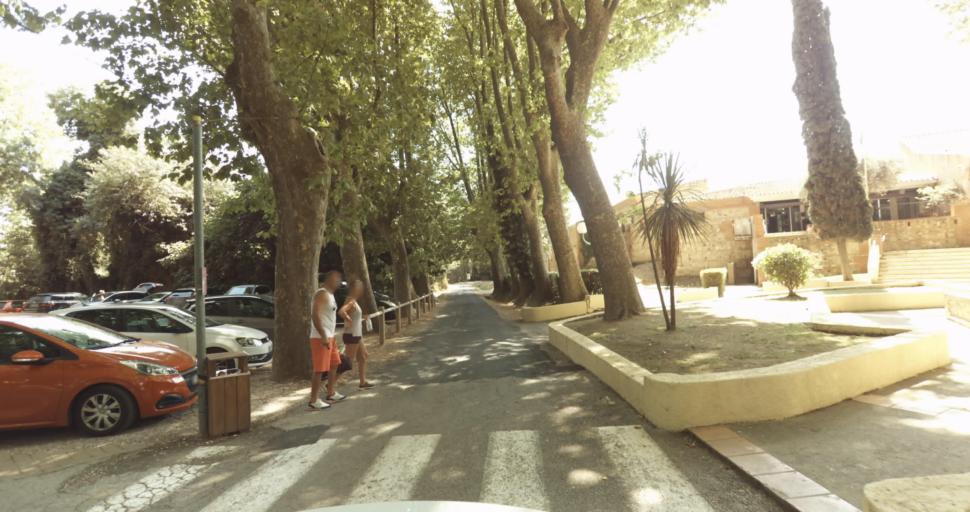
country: FR
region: Languedoc-Roussillon
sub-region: Departement des Pyrenees-Orientales
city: Saint-Cyprien-Plage
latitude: 42.6052
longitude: 3.0297
